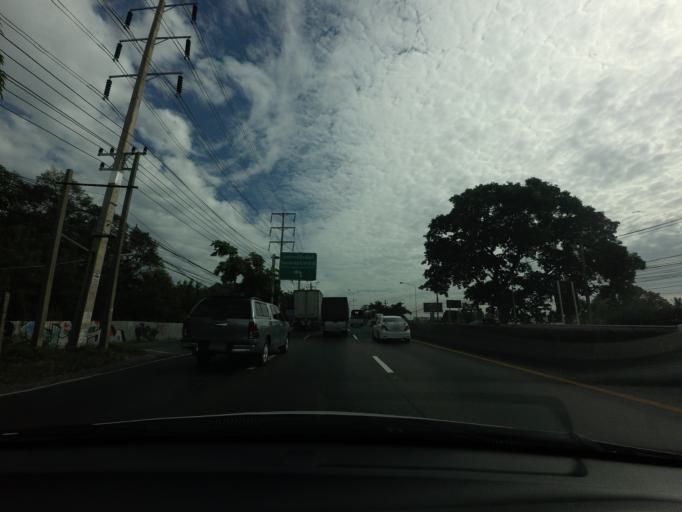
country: TH
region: Pathum Thani
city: Thanyaburi
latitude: 14.0095
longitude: 100.7090
